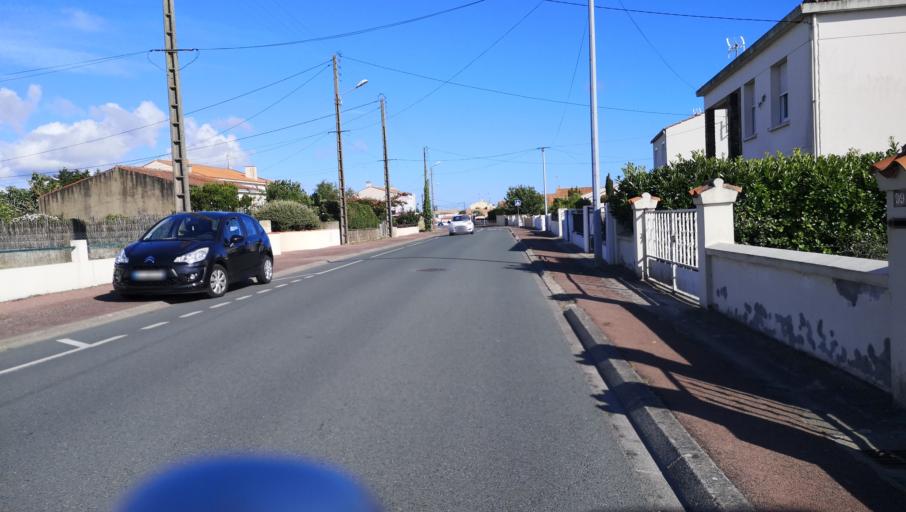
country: FR
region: Pays de la Loire
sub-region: Departement de la Vendee
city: Les Sables-d'Olonne
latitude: 46.5119
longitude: -1.7884
